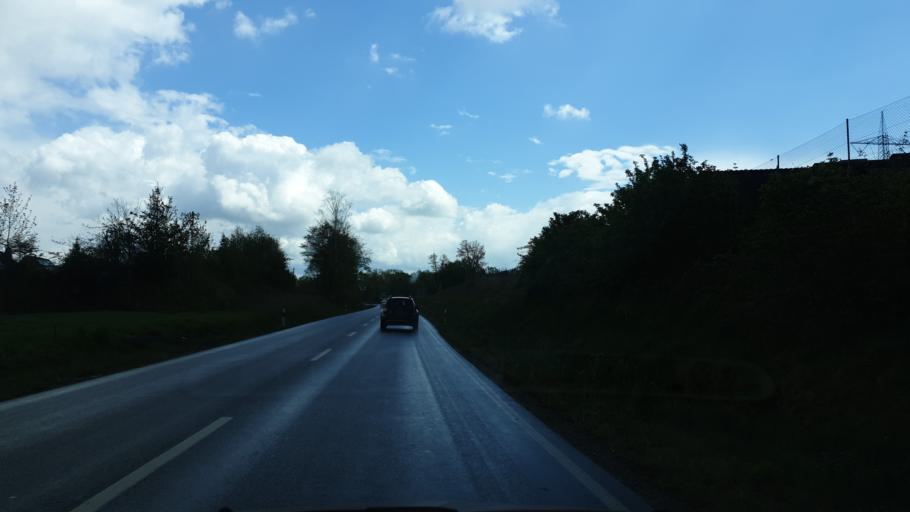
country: DE
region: Saxony
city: Neukirchen
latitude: 50.8105
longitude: 12.8165
